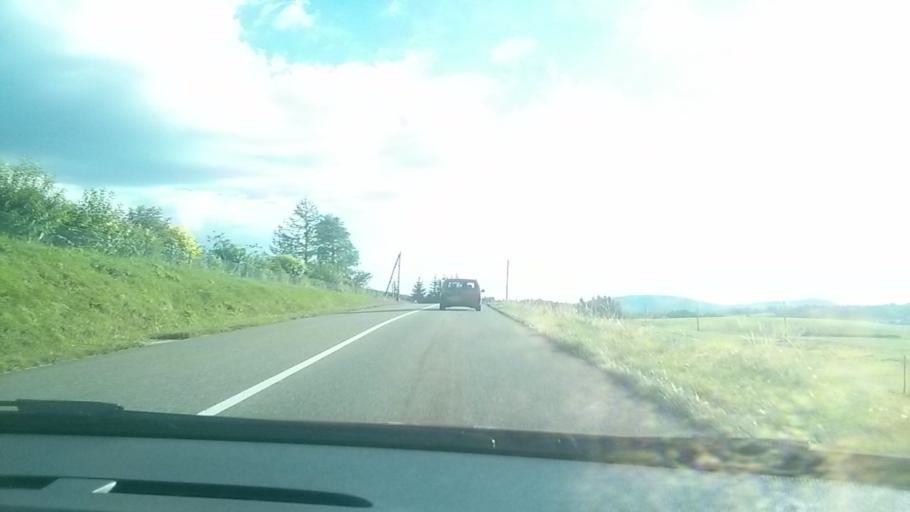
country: FR
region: Franche-Comte
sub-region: Departement du Jura
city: Les Rousses
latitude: 46.4950
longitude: 6.0958
